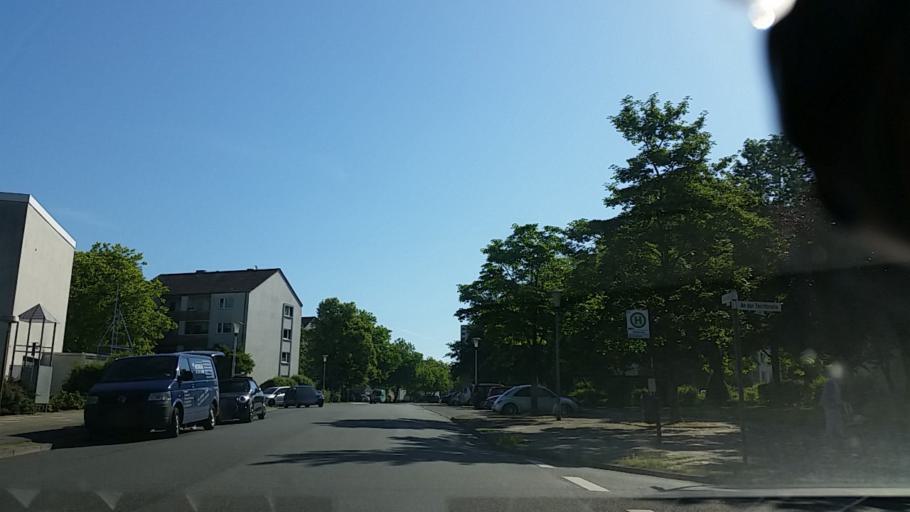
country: DE
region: Lower Saxony
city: Wolfsburg
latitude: 52.4440
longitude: 10.8083
